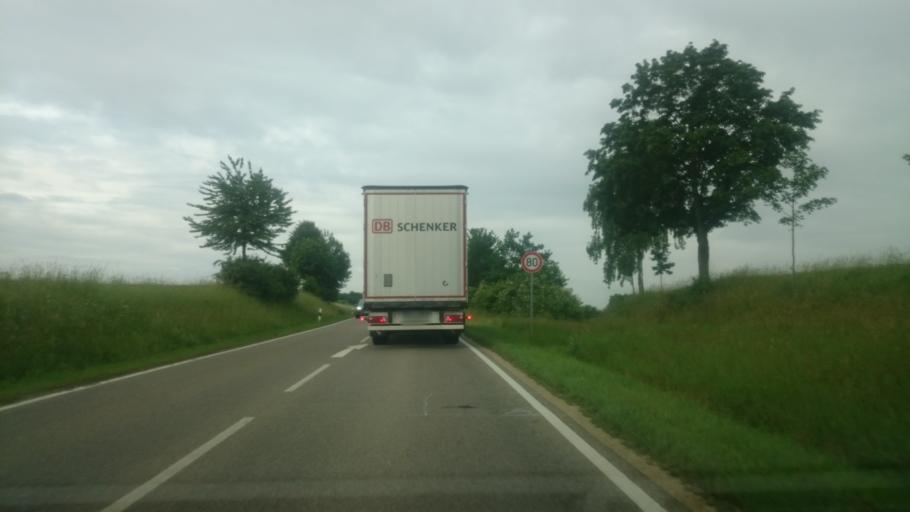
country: DE
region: Bavaria
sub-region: Upper Bavaria
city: Brunnen
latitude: 48.6343
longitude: 11.3250
